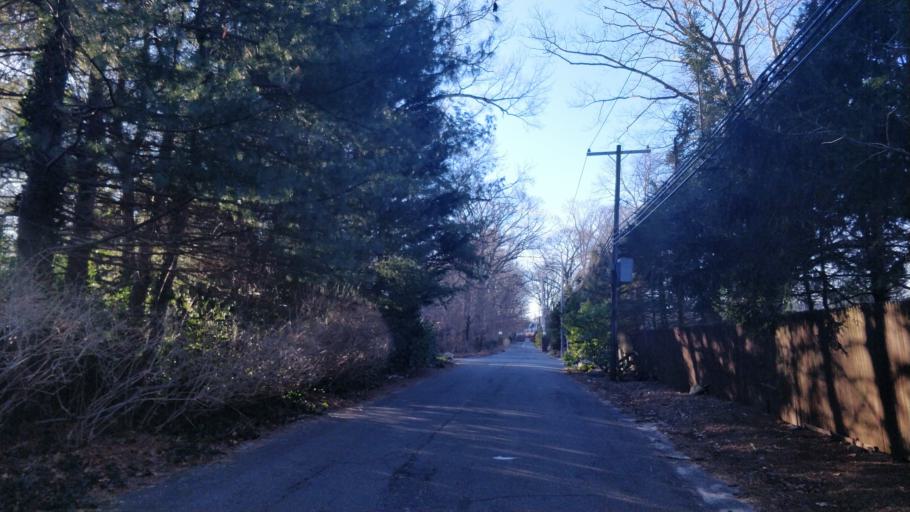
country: US
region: New York
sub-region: Nassau County
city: Glen Cove
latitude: 40.8760
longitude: -73.6491
